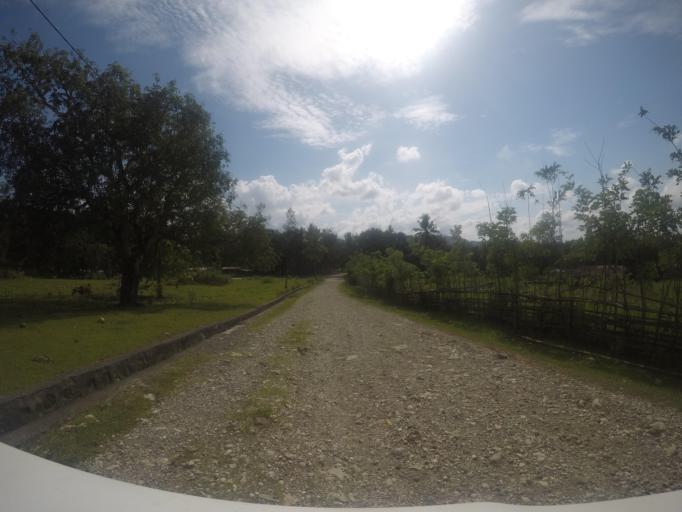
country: TL
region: Viqueque
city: Viqueque
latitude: -8.8533
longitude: 126.3574
